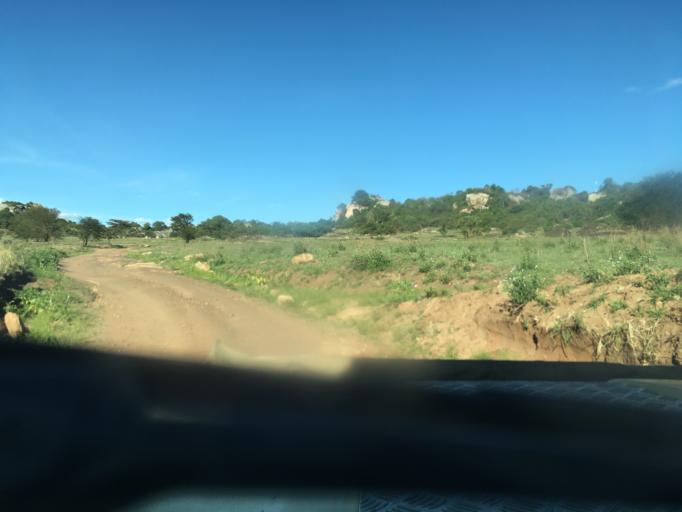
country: TZ
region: Mara
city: Mugumu
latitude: -1.9979
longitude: 35.1628
